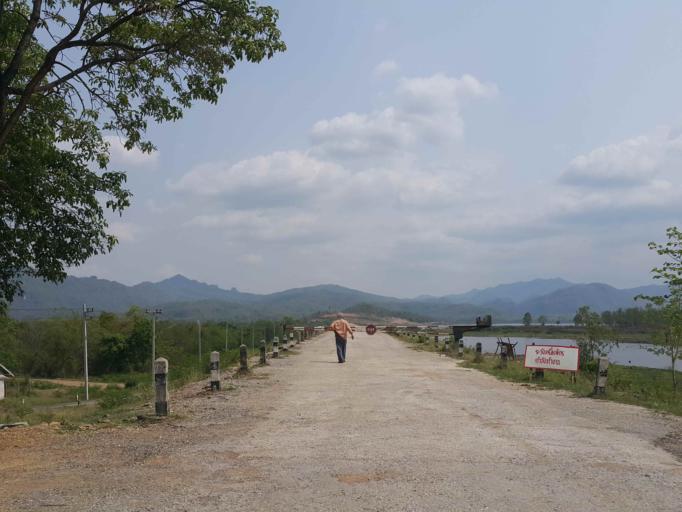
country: TH
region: Sukhothai
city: Thung Saliam
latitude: 17.3275
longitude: 99.4217
